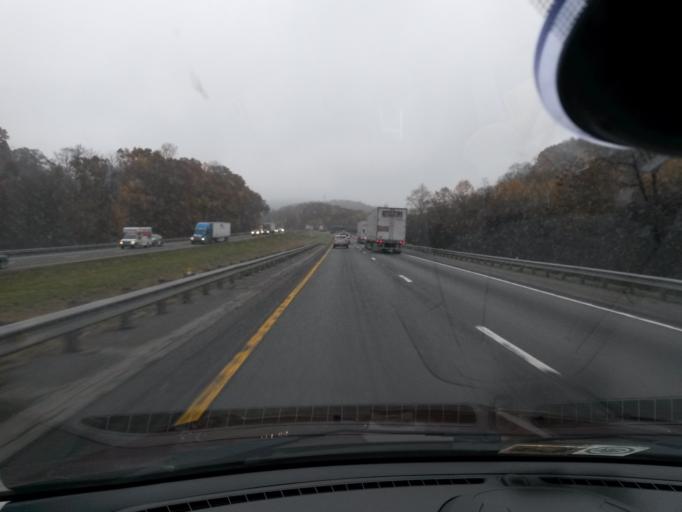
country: US
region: Virginia
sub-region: Montgomery County
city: Shawsville
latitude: 37.2500
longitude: -80.1909
